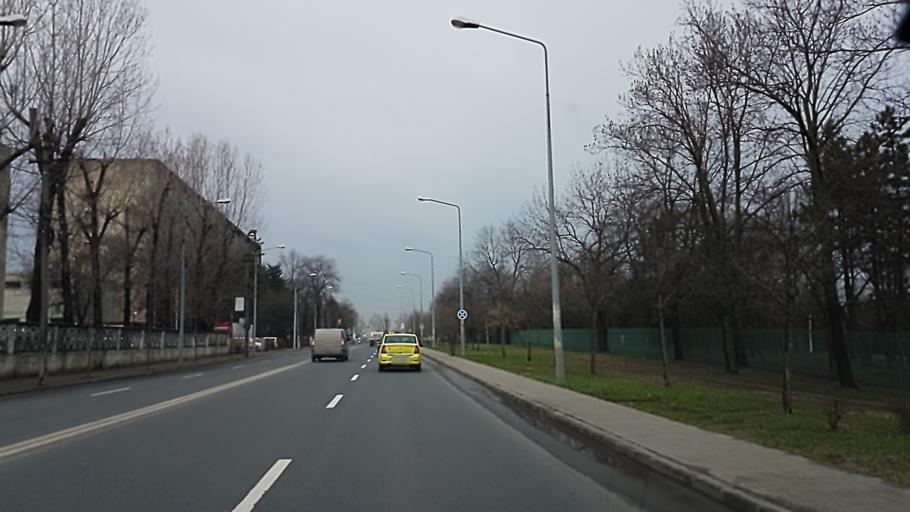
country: RO
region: Ilfov
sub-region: Comuna Pantelimon
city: Pantelimon
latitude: 44.4391
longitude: 26.1952
